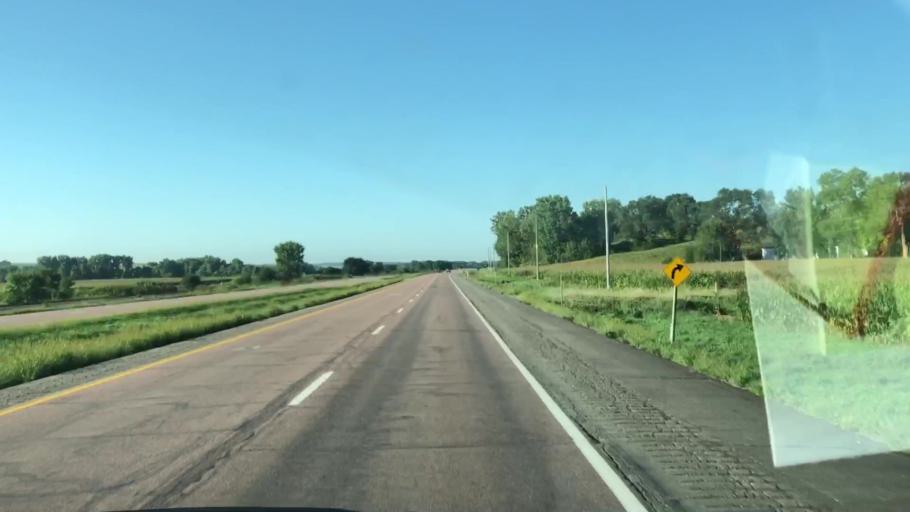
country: US
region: Iowa
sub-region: Woodbury County
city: Sioux City
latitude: 42.5888
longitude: -96.3078
